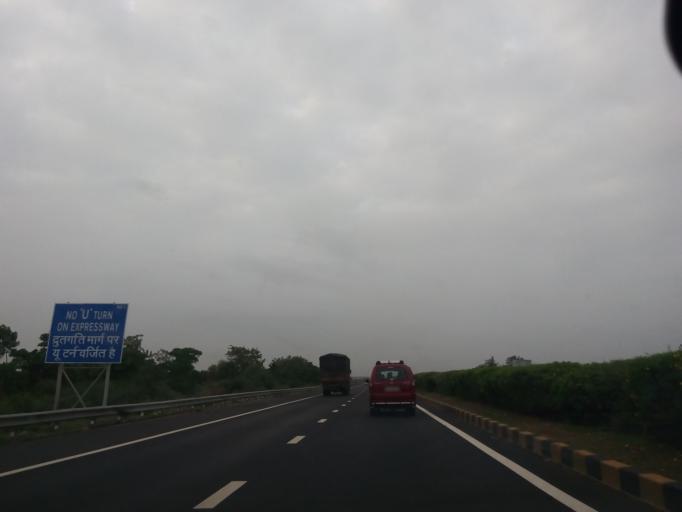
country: IN
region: Gujarat
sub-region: Kheda
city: Nadiad
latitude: 22.7757
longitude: 72.8487
